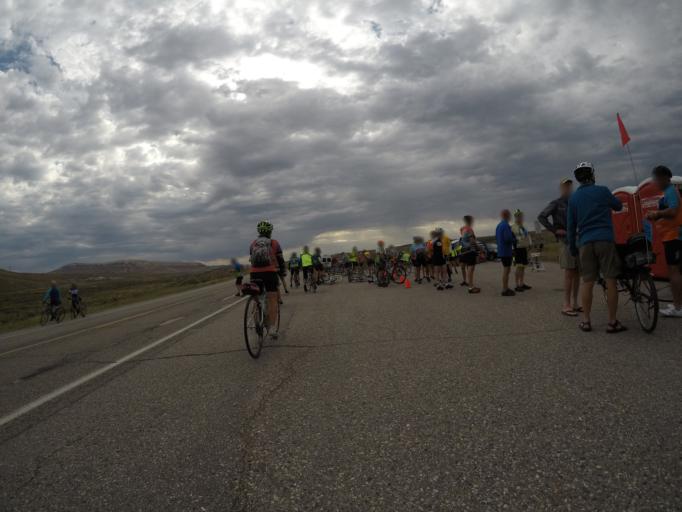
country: US
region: Wyoming
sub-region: Lincoln County
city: Kemmerer
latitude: 41.8176
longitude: -110.8041
